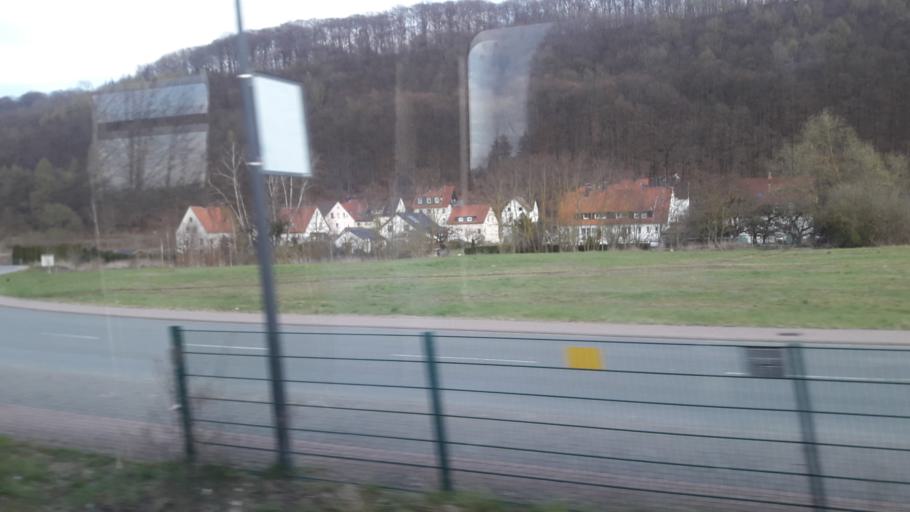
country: DE
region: North Rhine-Westphalia
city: Marsberg
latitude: 51.4667
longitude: 8.8599
